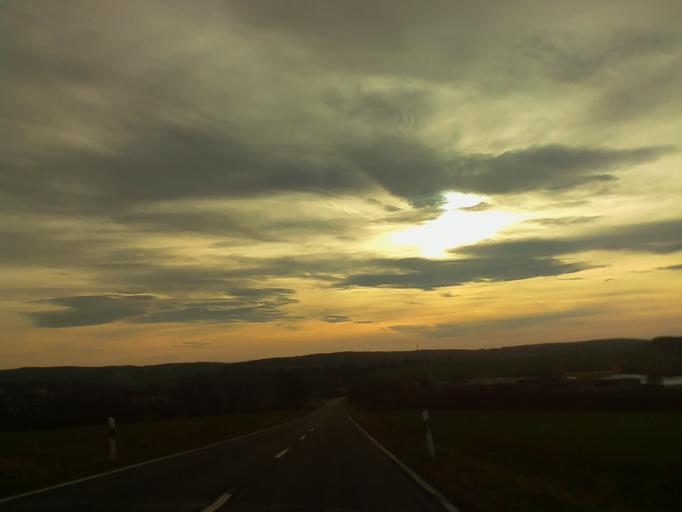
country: DE
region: Thuringia
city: Ruttersdorf-Lotschen
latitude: 50.8760
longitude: 11.7292
